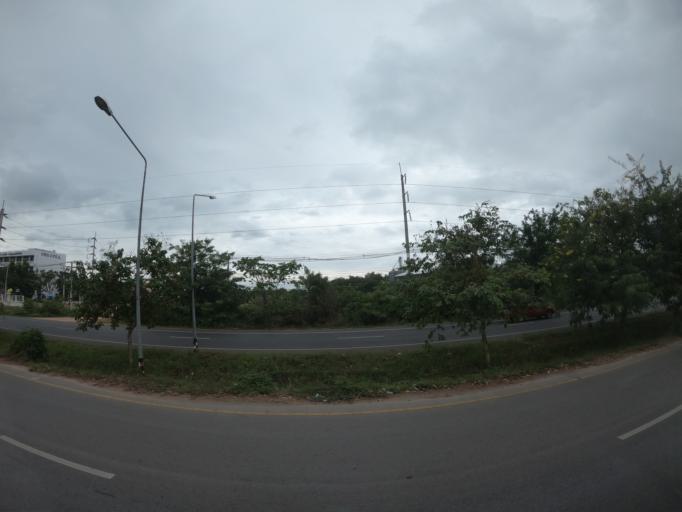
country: TH
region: Roi Et
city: Roi Et
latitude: 16.0445
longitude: 103.6277
